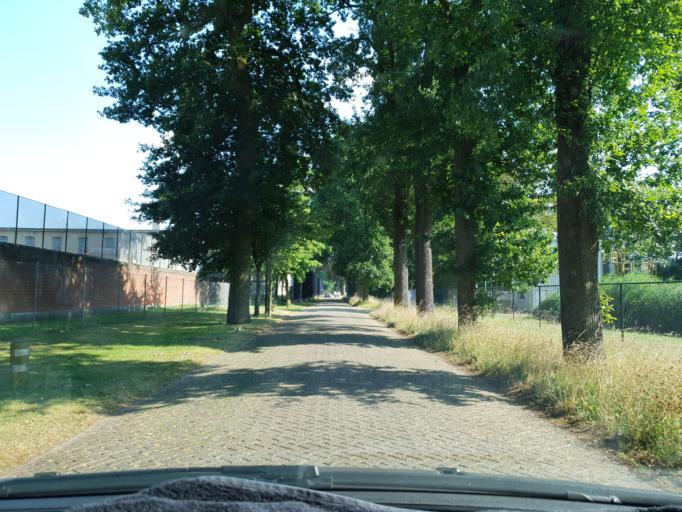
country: BE
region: Flanders
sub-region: Provincie Antwerpen
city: Merksplas
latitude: 51.3581
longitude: 4.8288
